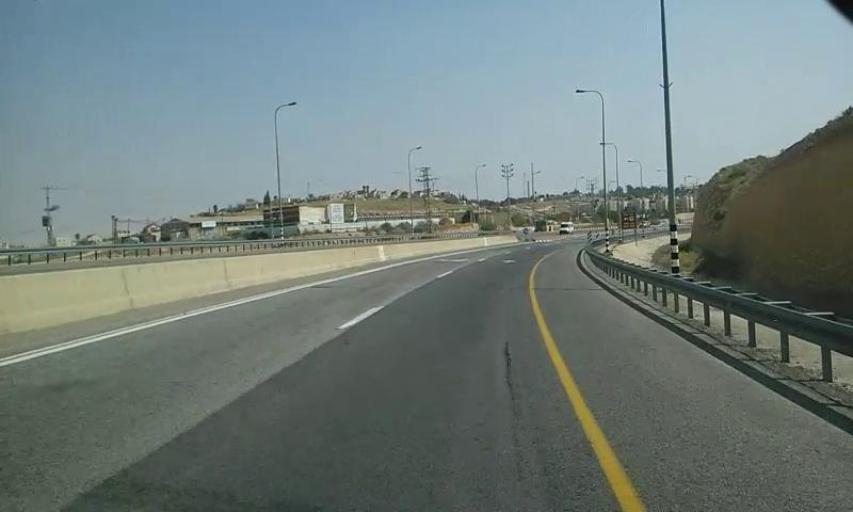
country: PS
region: West Bank
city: Jericho
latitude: 31.8201
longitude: 35.3888
